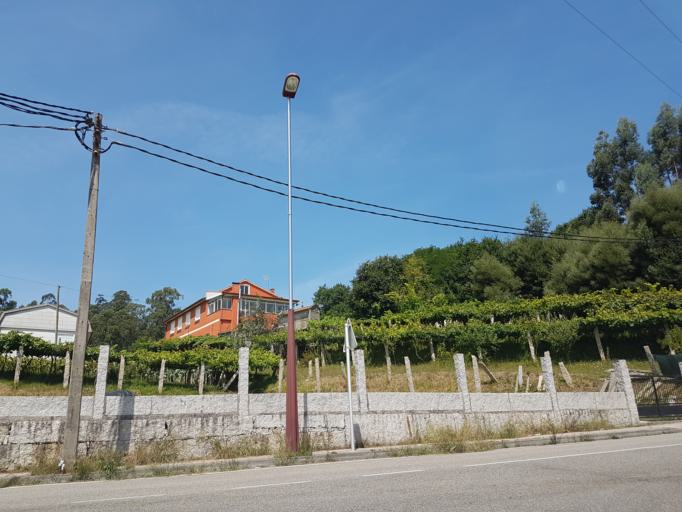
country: ES
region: Galicia
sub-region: Provincia de Pontevedra
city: Redondela
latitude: 42.2230
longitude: -8.6212
